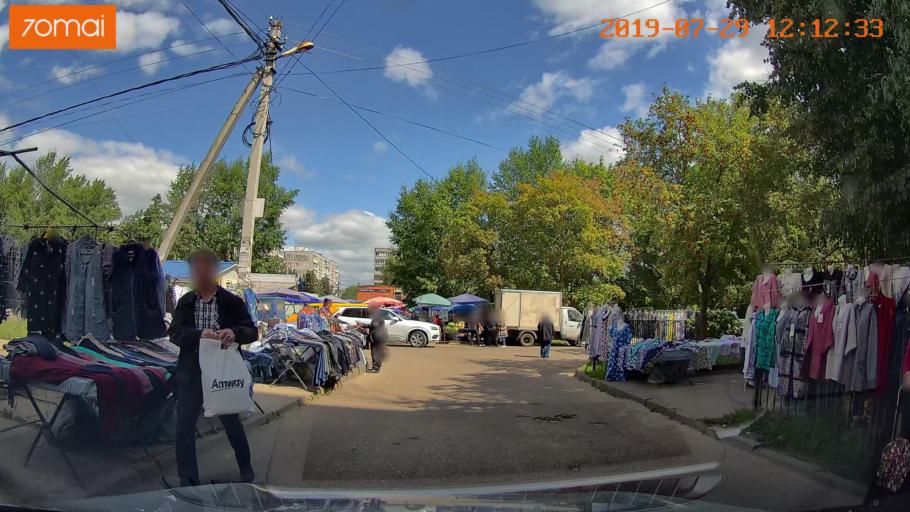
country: RU
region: Moskovskaya
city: Voskresensk
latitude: 55.3146
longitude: 38.6493
